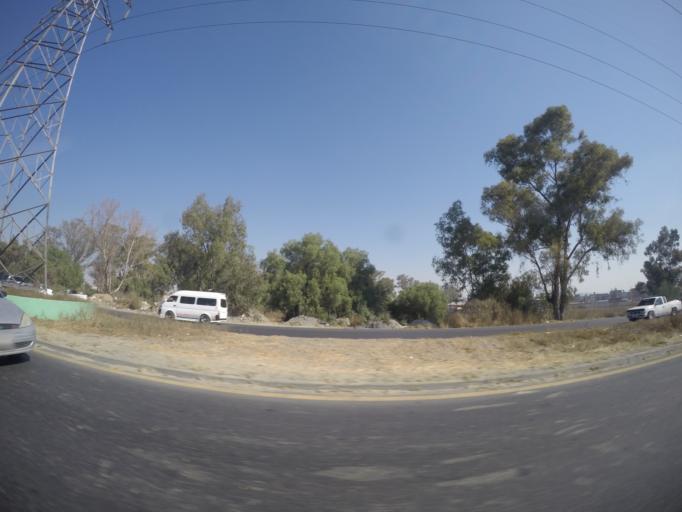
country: MX
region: Mexico
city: Santo Tomas Chiconautla
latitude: 19.6141
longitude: -99.0139
